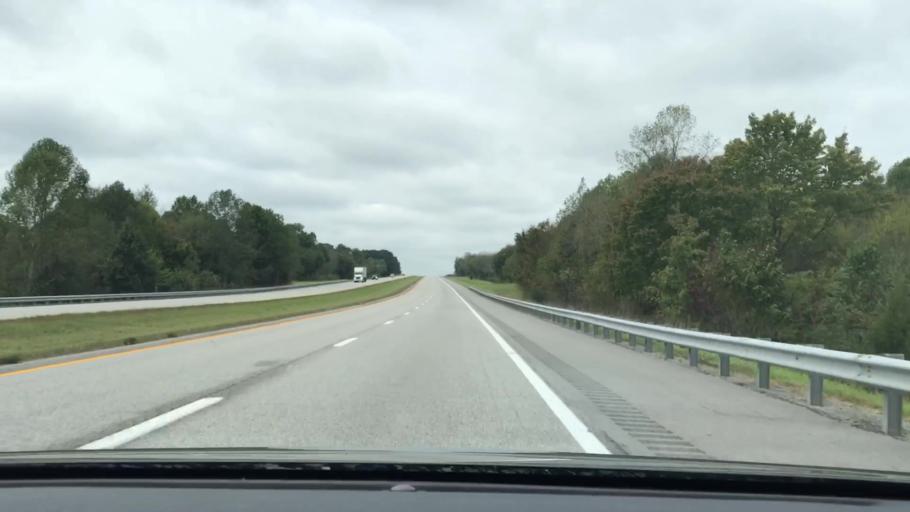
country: US
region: Kentucky
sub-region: Russell County
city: Russell Springs
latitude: 37.0730
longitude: -85.0019
